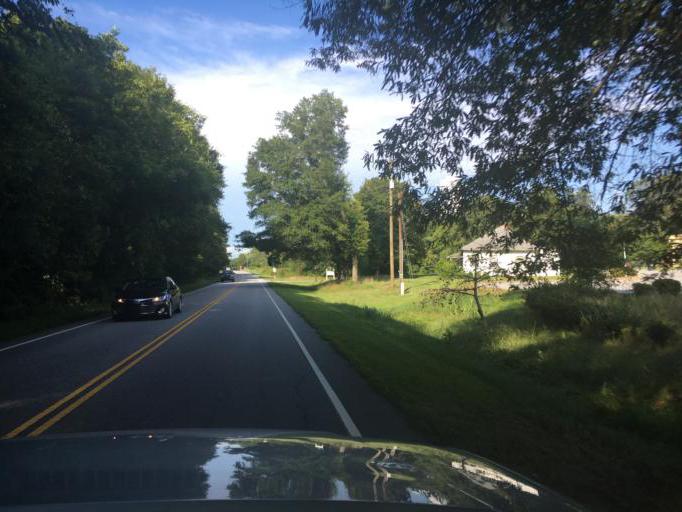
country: US
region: South Carolina
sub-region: Greenville County
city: Mauldin
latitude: 34.7781
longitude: -82.2802
